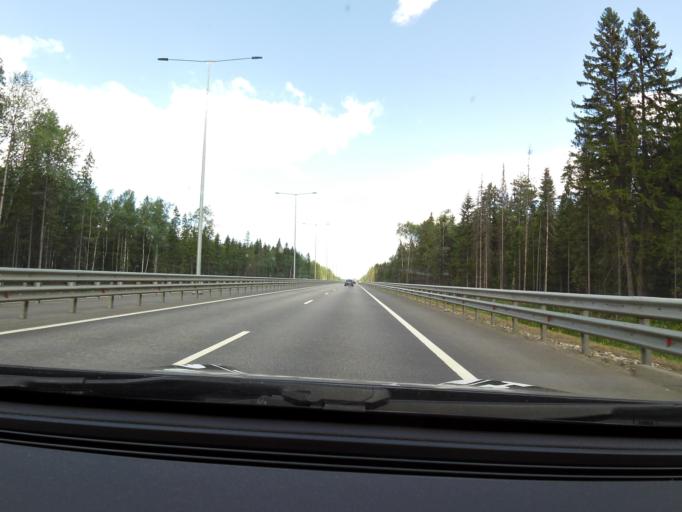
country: RU
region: Tverskaya
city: Vydropuzhsk
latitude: 57.3026
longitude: 34.7702
